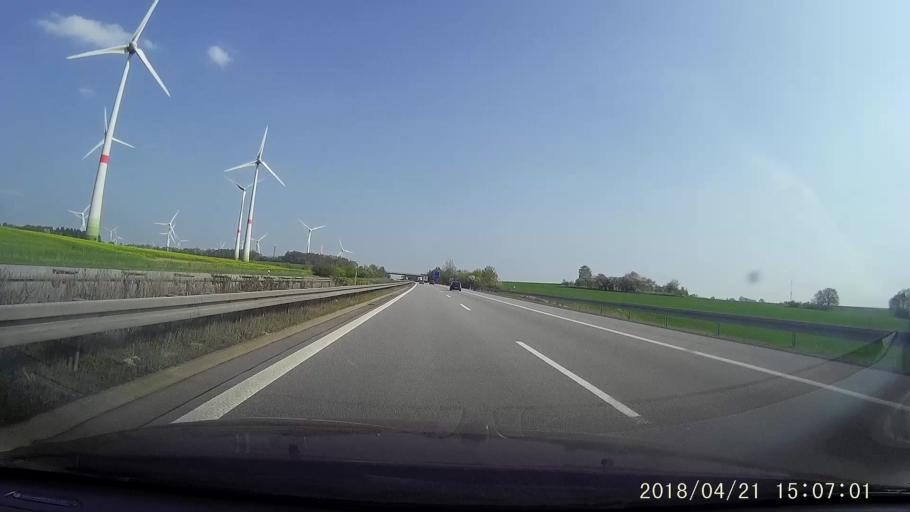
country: DE
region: Saxony
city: Goerlitz
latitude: 51.2046
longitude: 14.9498
